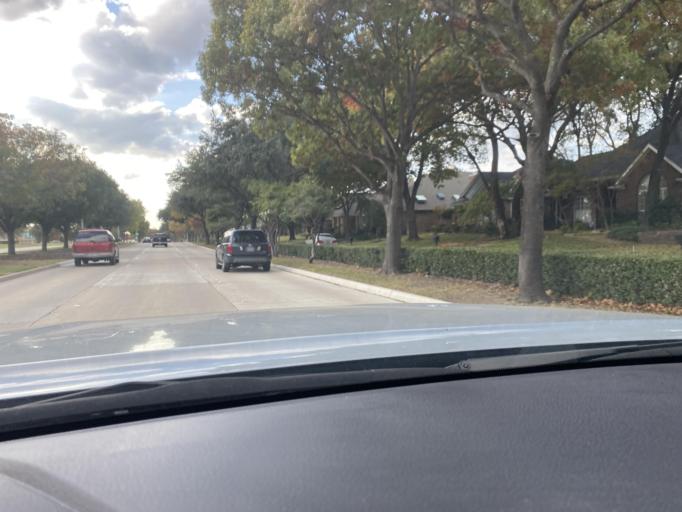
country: US
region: Texas
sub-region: Dallas County
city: Addison
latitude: 33.0167
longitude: -96.8019
